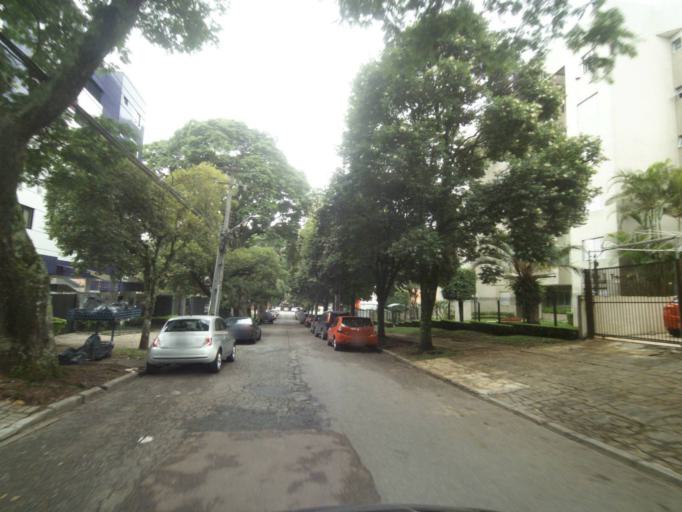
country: BR
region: Parana
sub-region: Curitiba
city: Curitiba
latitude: -25.4125
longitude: -49.2605
